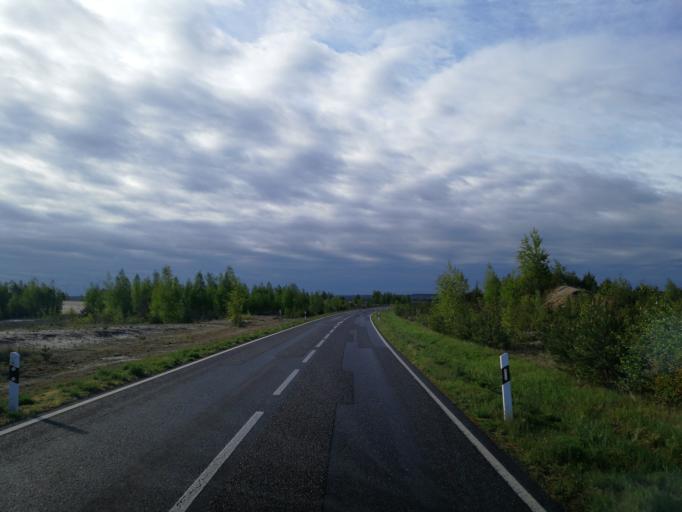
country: DE
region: Brandenburg
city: Sallgast
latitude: 51.5763
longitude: 13.7738
